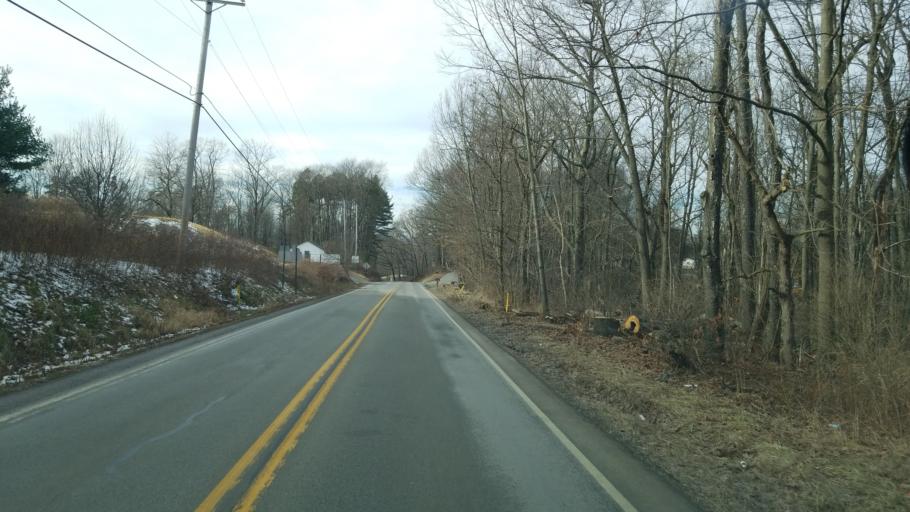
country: US
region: Pennsylvania
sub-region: Jefferson County
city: Punxsutawney
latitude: 40.9050
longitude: -79.0105
